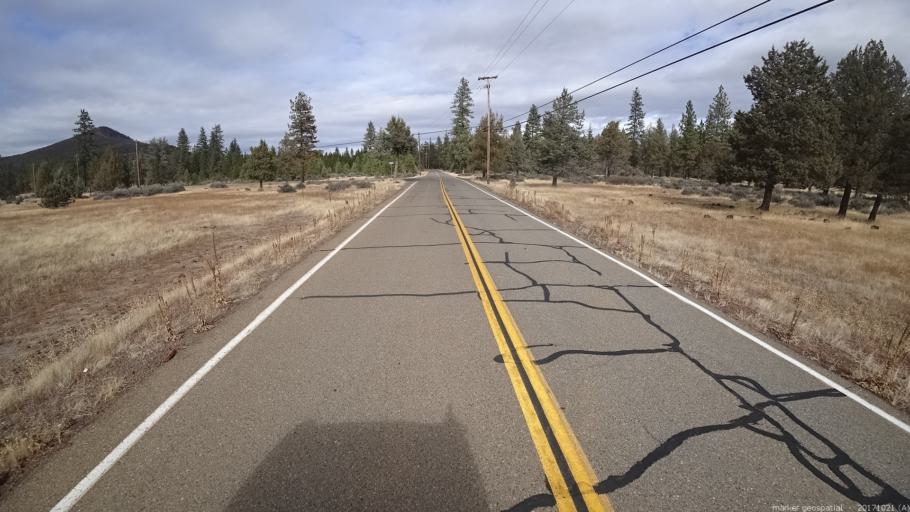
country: US
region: California
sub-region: Shasta County
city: Burney
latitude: 40.9246
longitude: -121.6461
